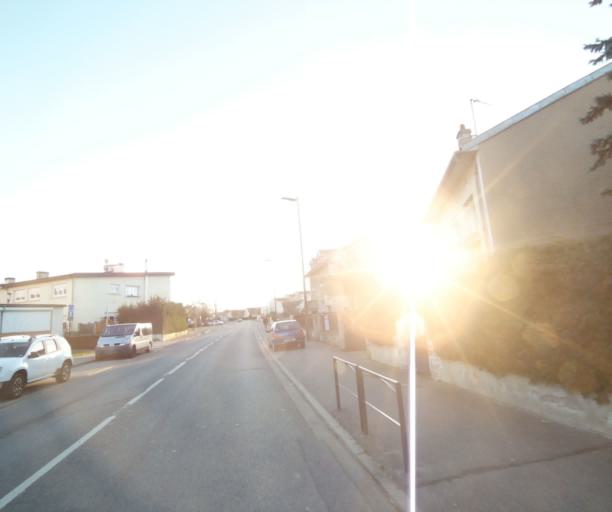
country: FR
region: Lorraine
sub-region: Departement de Meurthe-et-Moselle
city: Pulnoy
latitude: 48.7004
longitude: 6.2563
